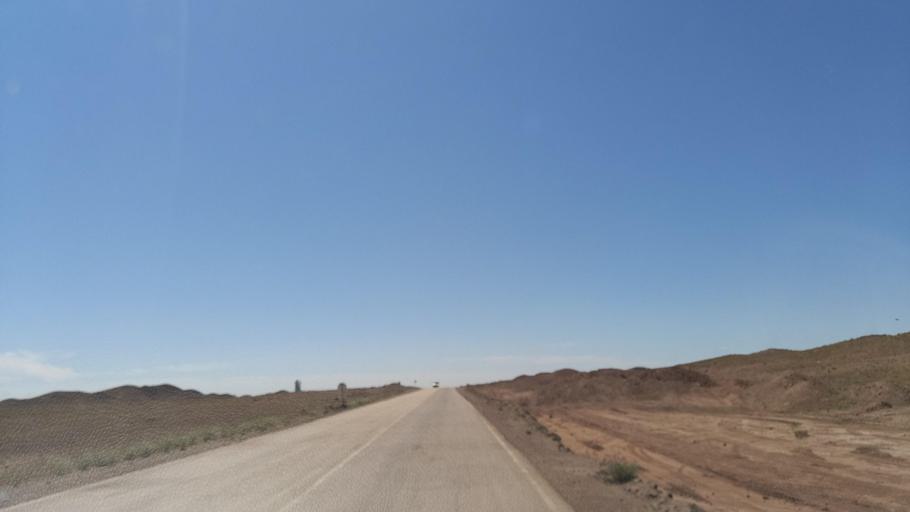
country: KZ
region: Zhambyl
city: Mynaral
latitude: 45.4094
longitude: 73.6309
